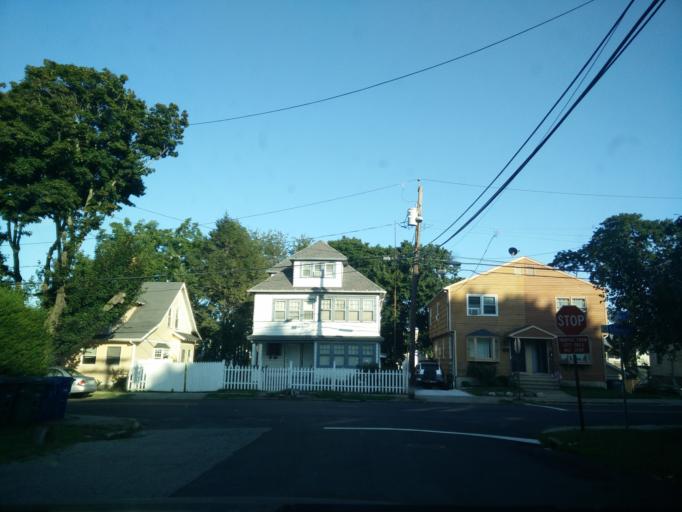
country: US
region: Connecticut
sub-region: Fairfield County
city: Bridgeport
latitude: 41.1618
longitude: -73.2209
